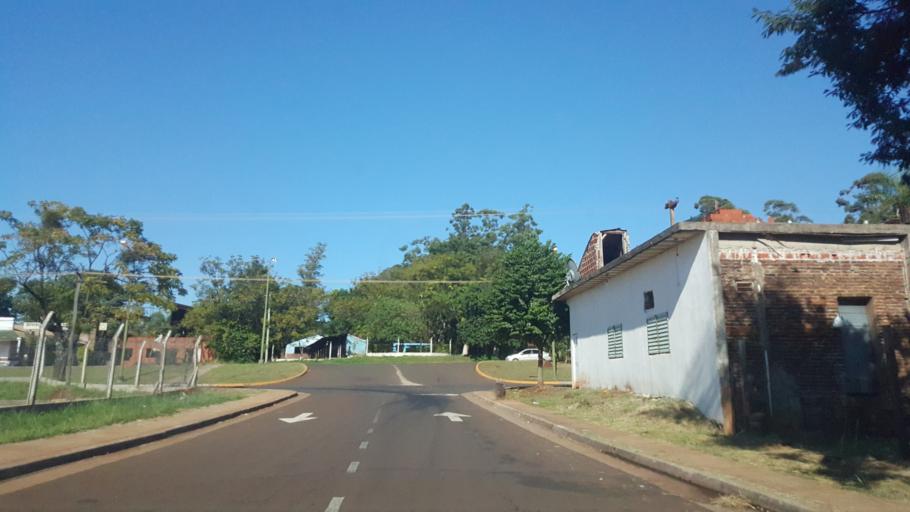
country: AR
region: Misiones
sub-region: Departamento de Capital
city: Posadas
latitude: -27.4130
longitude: -55.9000
